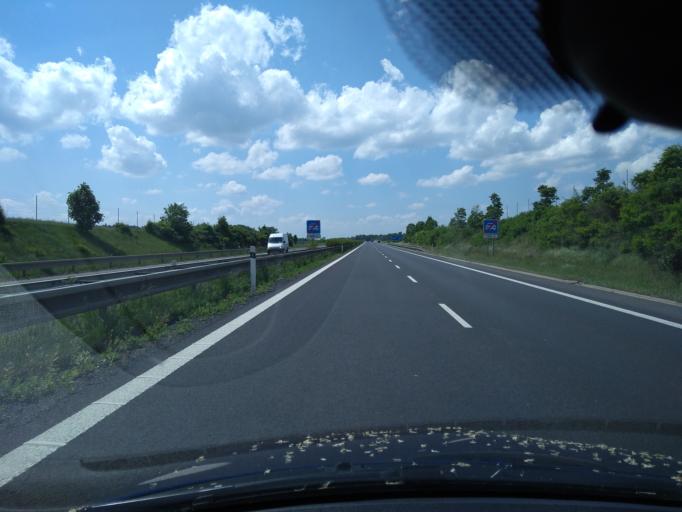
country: CZ
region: Plzensky
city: Chlumcany
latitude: 49.6651
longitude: 13.3479
